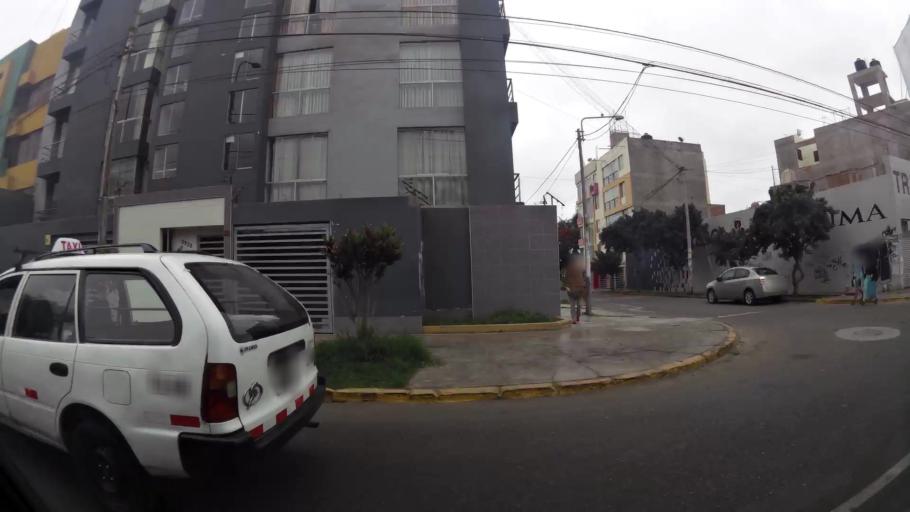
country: PE
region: La Libertad
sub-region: Provincia de Trujillo
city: Trujillo
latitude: -8.1250
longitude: -79.0377
